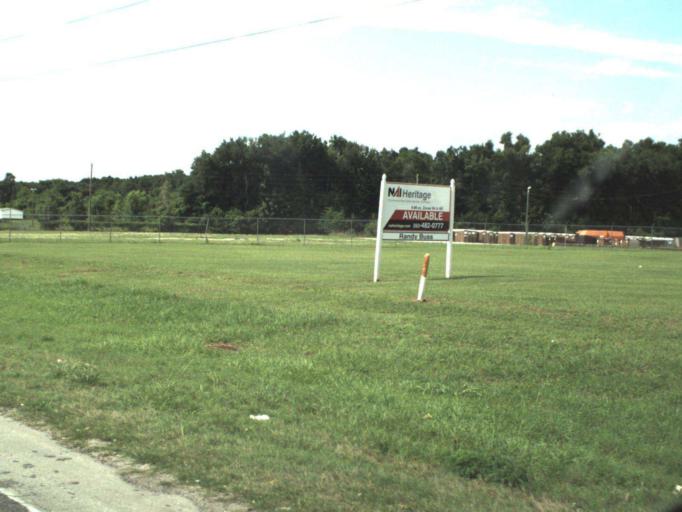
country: US
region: Florida
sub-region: Marion County
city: Ocala
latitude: 29.1368
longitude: -82.1086
